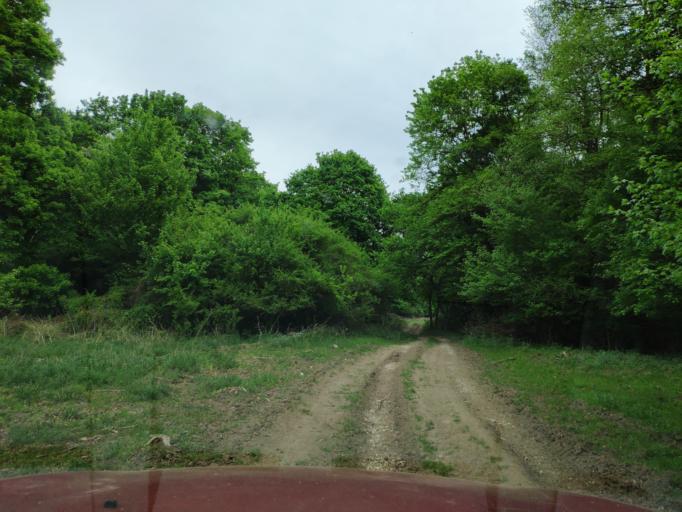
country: SK
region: Banskobystricky
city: Revuca
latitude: 48.5198
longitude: 20.1541
